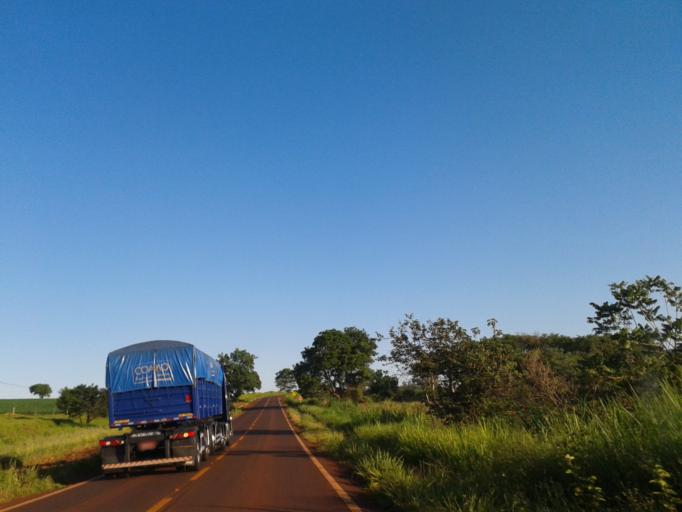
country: BR
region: Minas Gerais
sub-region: Capinopolis
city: Capinopolis
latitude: -18.7136
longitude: -49.5584
